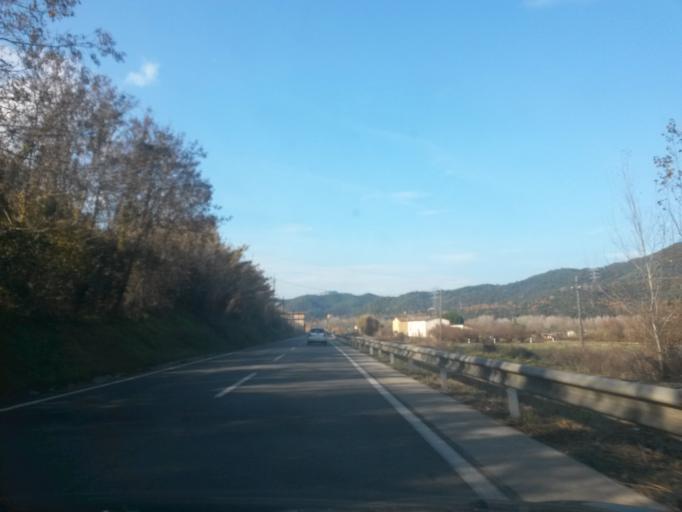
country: ES
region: Catalonia
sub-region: Provincia de Girona
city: Sant Gregori
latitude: 41.9746
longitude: 2.7126
